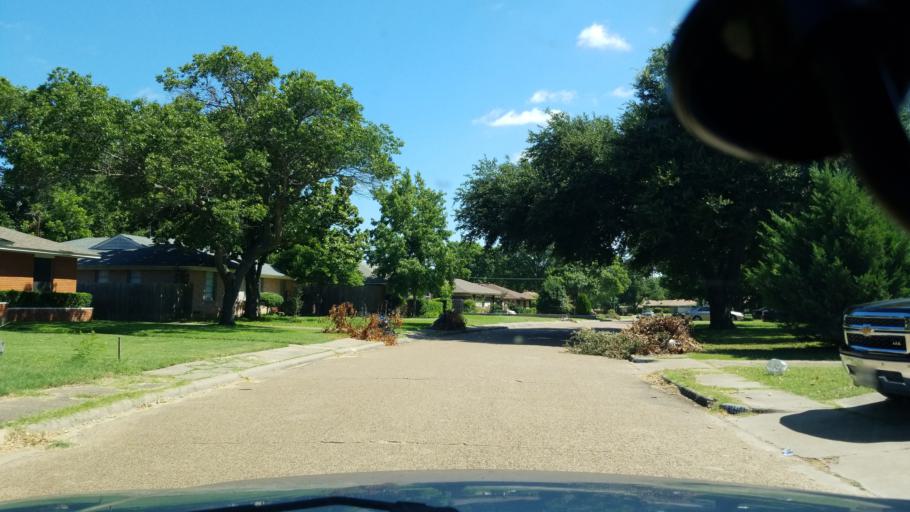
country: US
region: Texas
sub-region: Dallas County
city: Cockrell Hill
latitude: 32.6842
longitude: -96.8312
